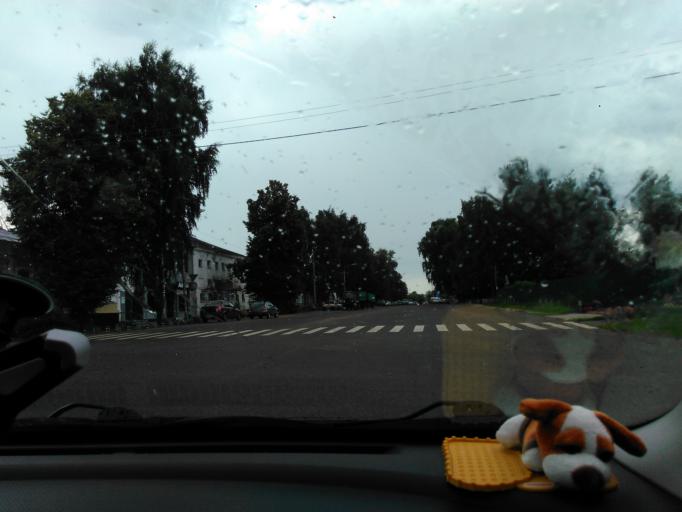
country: RU
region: Penza
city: Belinskiy
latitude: 52.9669
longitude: 43.4206
